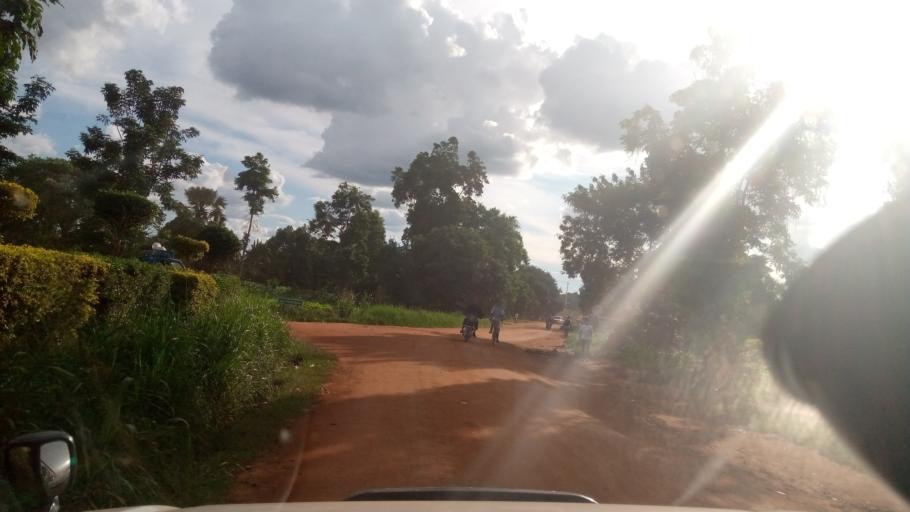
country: UG
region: Northern Region
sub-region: Lira District
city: Lira
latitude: 2.2275
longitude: 32.8976
